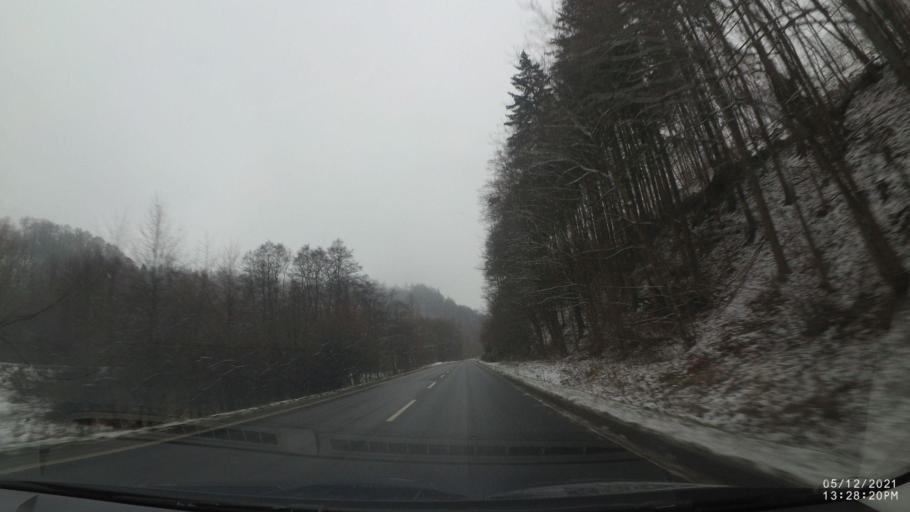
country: CZ
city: Hronov
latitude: 50.4994
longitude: 16.2018
